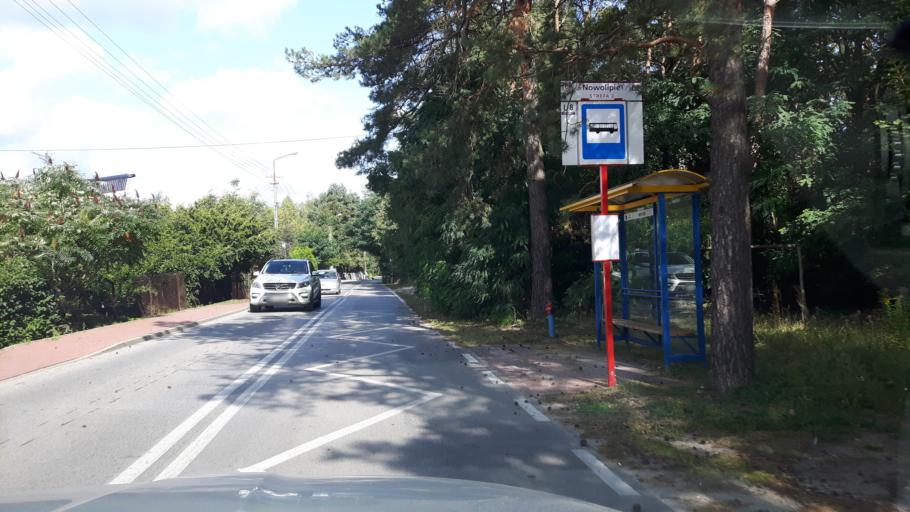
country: PL
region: Masovian Voivodeship
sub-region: Powiat legionowski
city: Bialobrzegi
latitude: 52.4227
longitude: 21.0508
